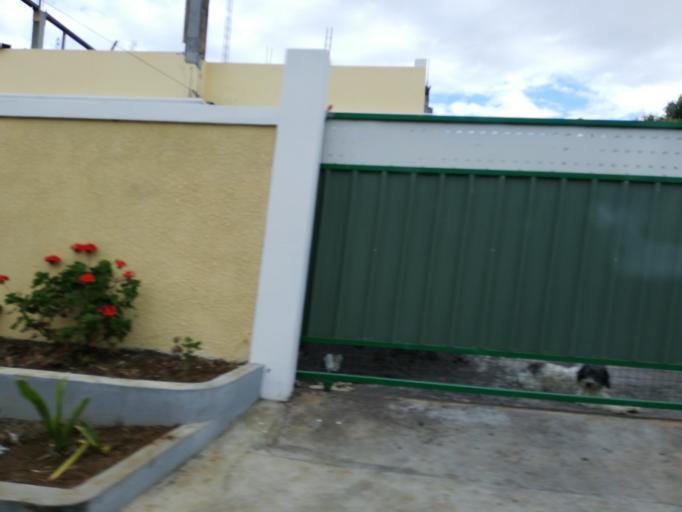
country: MU
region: Black River
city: Gros Cailloux
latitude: -20.2324
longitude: 57.4555
